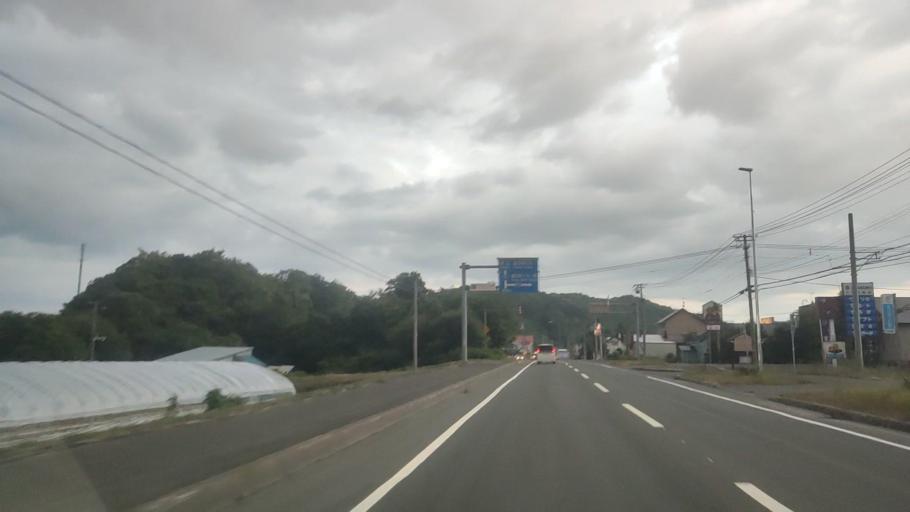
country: JP
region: Hokkaido
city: Shimo-furano
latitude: 43.3474
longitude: 142.3686
